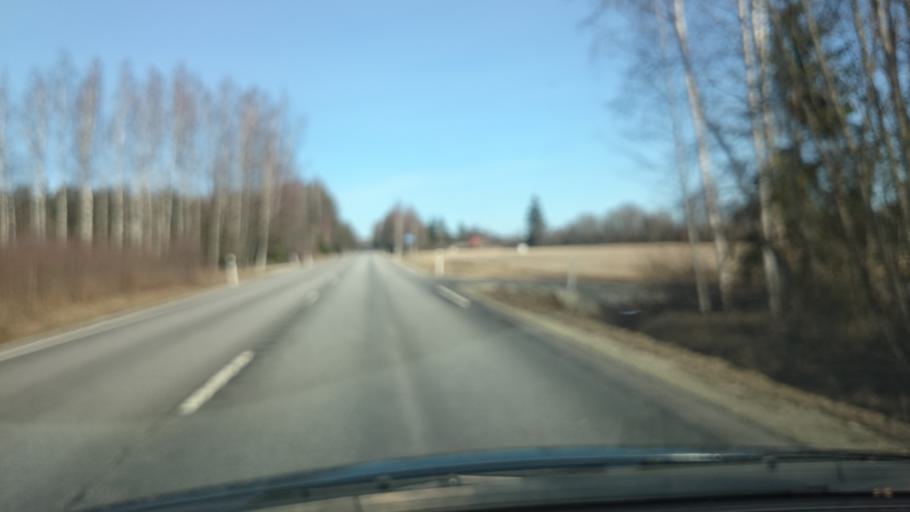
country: EE
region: Jaervamaa
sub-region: Tueri vald
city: Sarevere
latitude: 58.7065
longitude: 25.2651
